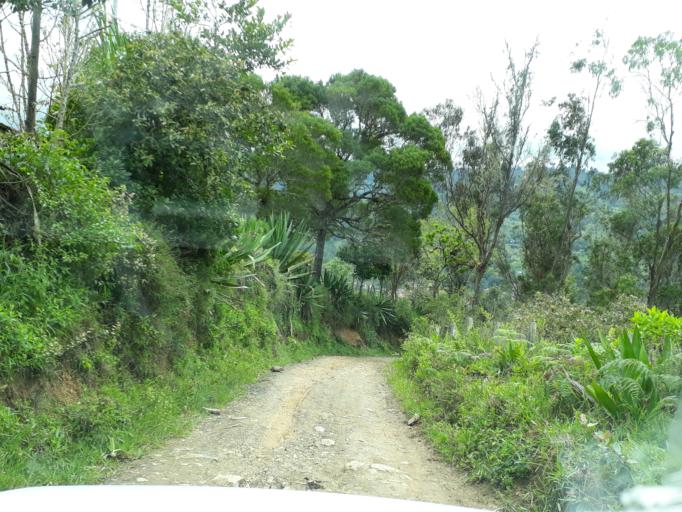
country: CO
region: Cundinamarca
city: Gacheta
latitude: 4.8082
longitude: -73.6455
